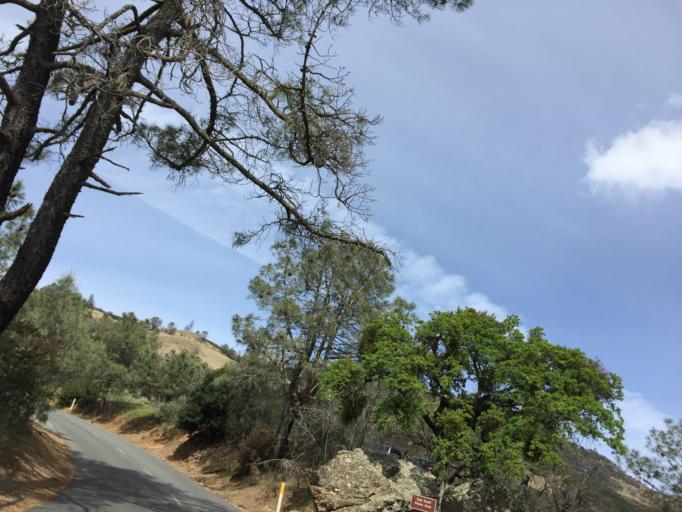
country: US
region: California
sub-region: Contra Costa County
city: Diablo
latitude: 37.8696
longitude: -121.9251
